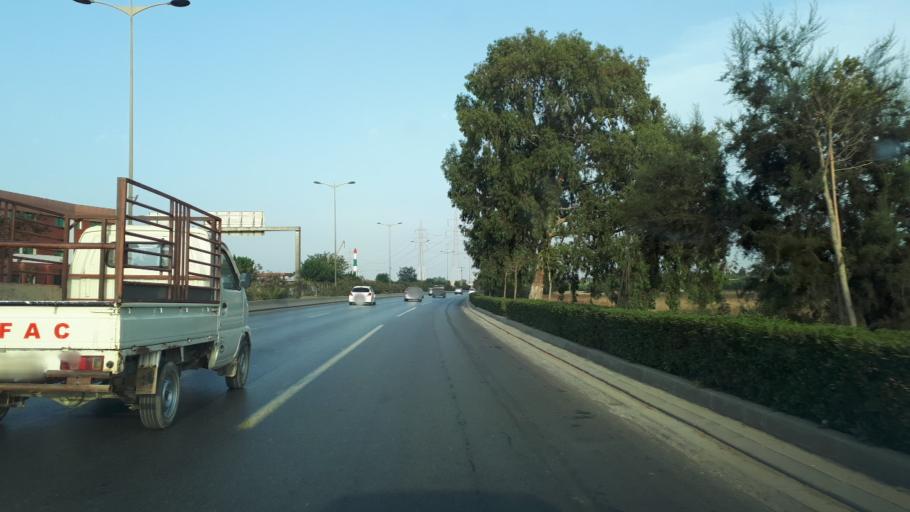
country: DZ
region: Alger
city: Bab Ezzouar
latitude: 36.7313
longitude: 3.2009
